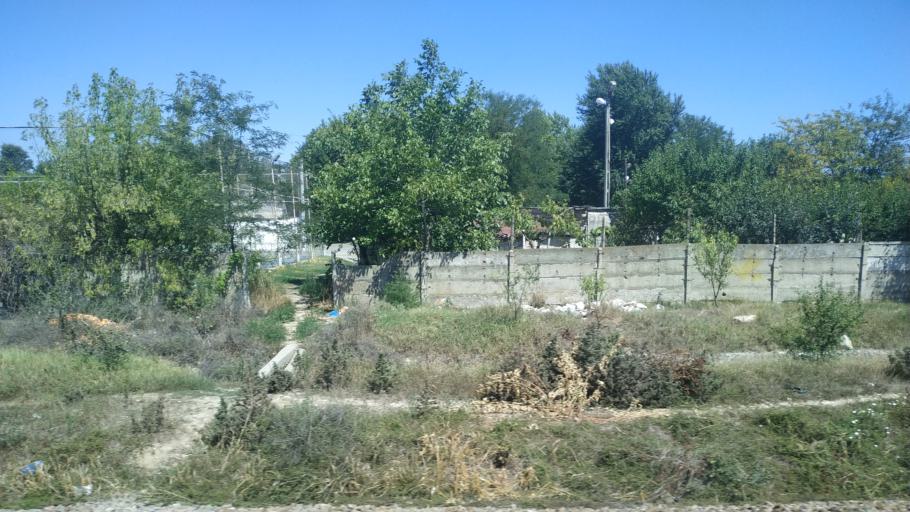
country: RO
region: Constanta
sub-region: Oras Murfatlar
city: Murfatlar
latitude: 44.1736
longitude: 28.4063
